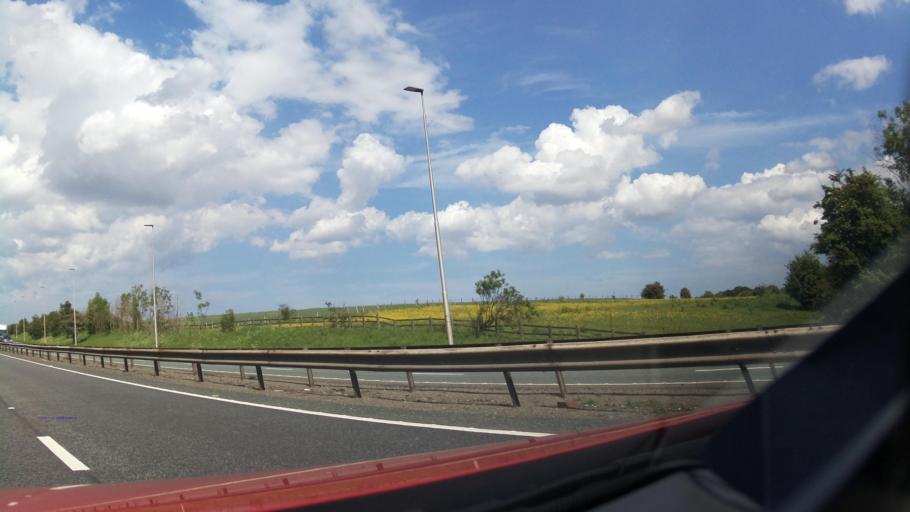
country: GB
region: England
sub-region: Redcar and Cleveland
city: Thornaby-on-Tees
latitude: 54.5221
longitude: -1.2800
